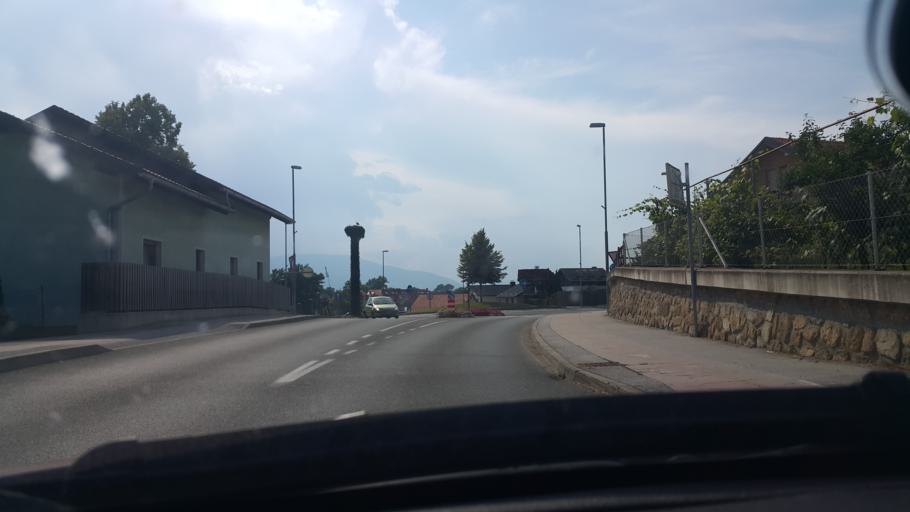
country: SI
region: Duplek
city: Spodnji Duplek
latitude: 46.5008
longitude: 15.7544
